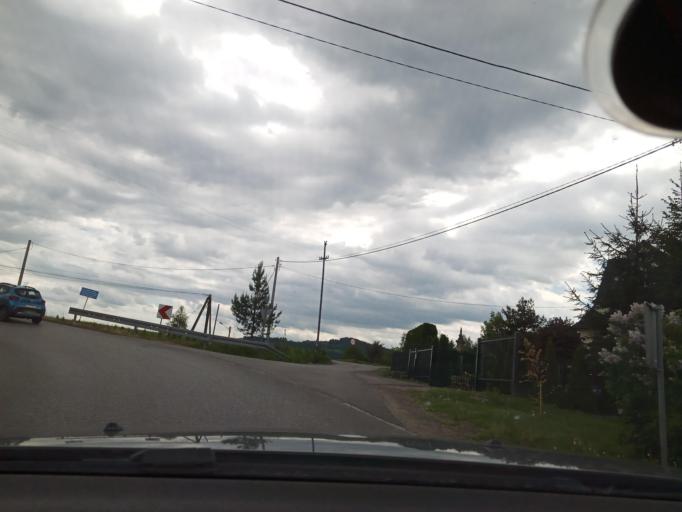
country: PL
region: Lesser Poland Voivodeship
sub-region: Powiat limanowski
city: Tymbark
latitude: 49.7720
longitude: 20.3366
